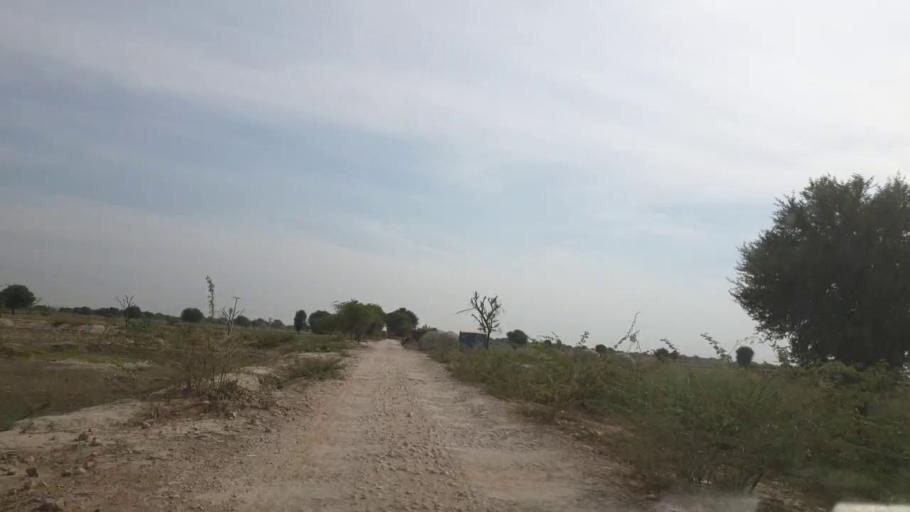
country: PK
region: Sindh
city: Nabisar
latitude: 25.0401
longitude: 69.5616
